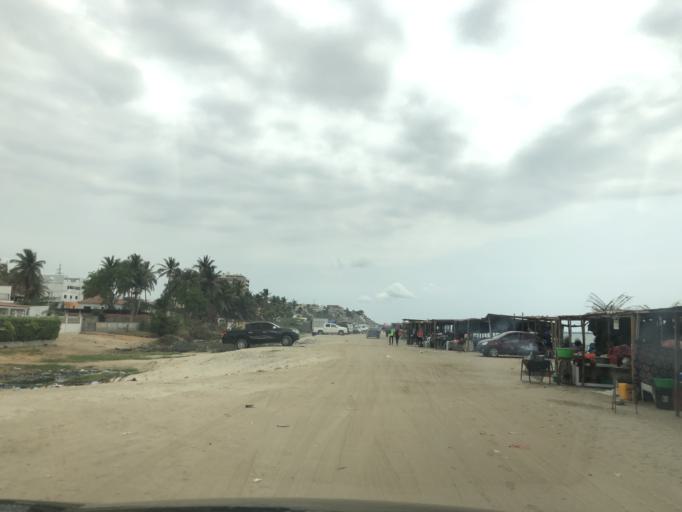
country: AO
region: Luanda
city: Luanda
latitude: -8.8737
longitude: 13.1920
